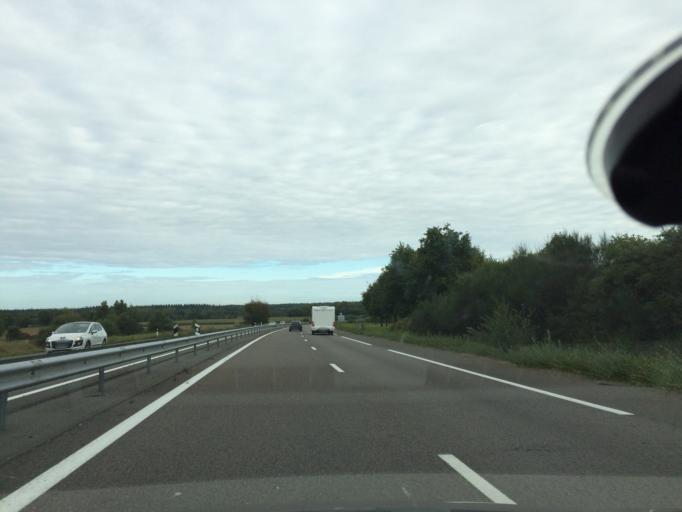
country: FR
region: Brittany
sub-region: Departement d'Ille-et-Vilaine
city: Saint-Pierre-de-Plesguen
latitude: 48.4453
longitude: -1.9249
